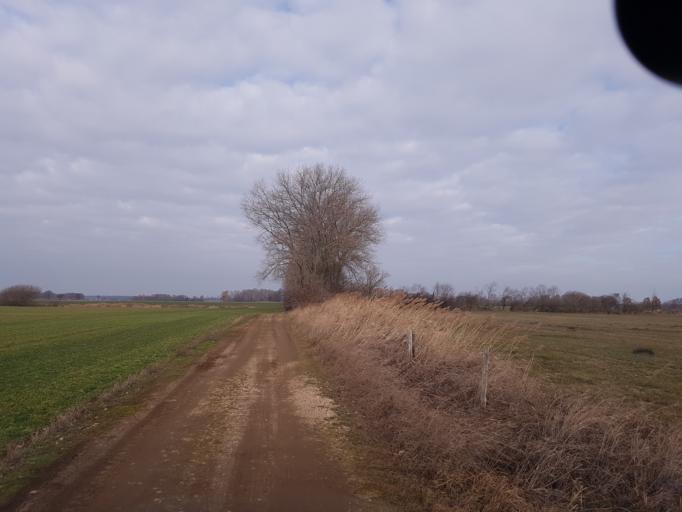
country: DE
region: Brandenburg
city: Doberlug-Kirchhain
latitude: 51.6656
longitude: 13.5642
